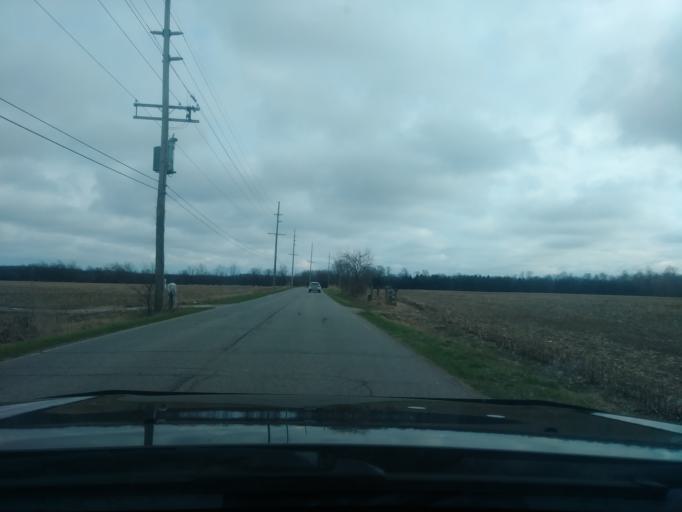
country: US
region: Indiana
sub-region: LaPorte County
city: LaPorte
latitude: 41.6398
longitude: -86.7980
